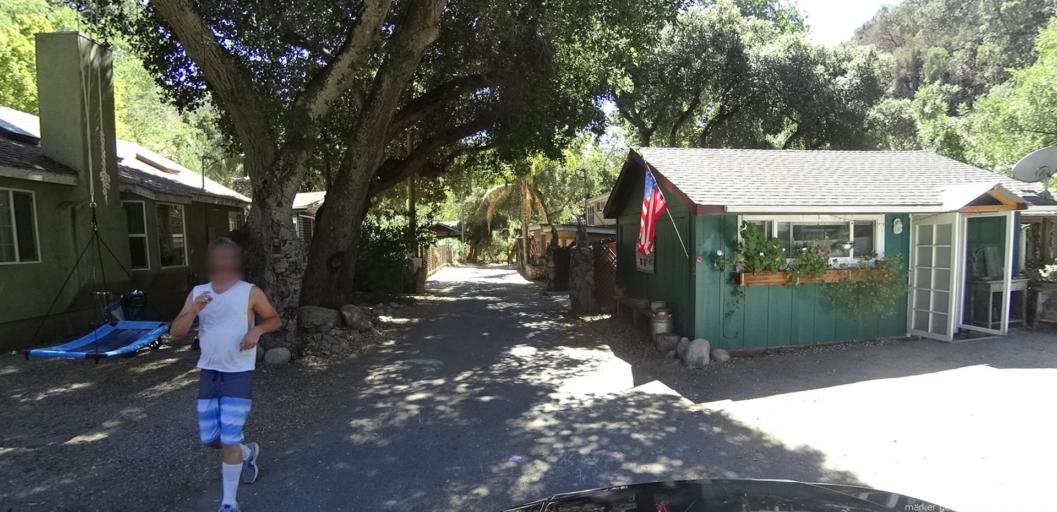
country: US
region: California
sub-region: Monterey County
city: Carmel Valley Village
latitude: 36.4706
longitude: -121.7162
